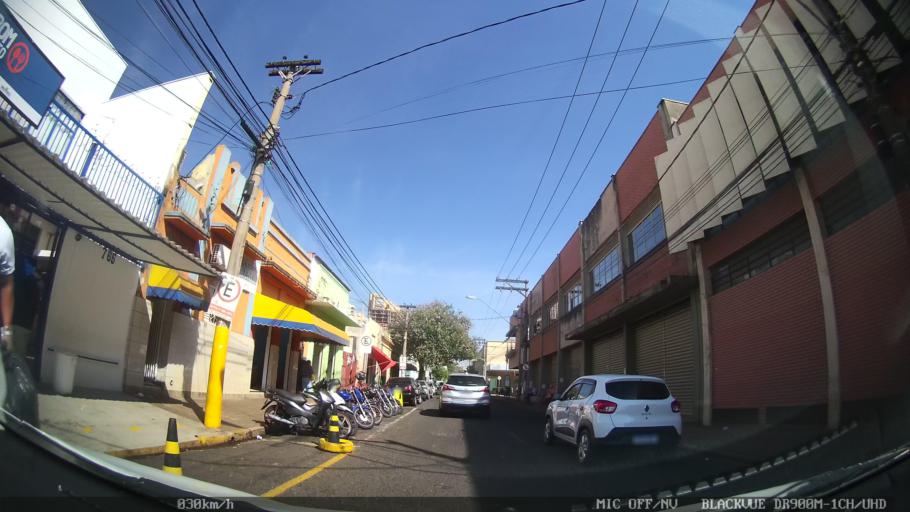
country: BR
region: Sao Paulo
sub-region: Ribeirao Preto
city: Ribeirao Preto
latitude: -21.1761
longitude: -47.8132
